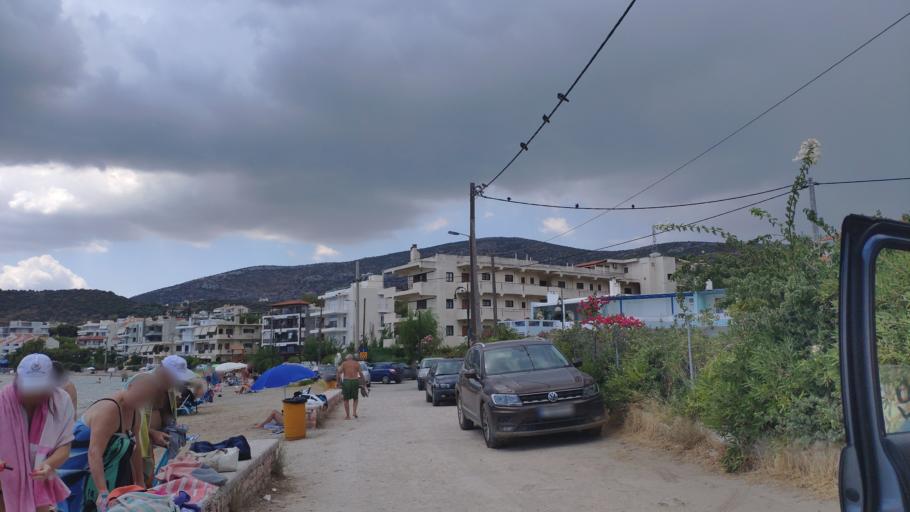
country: GR
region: Attica
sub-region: Nomarchia Anatolikis Attikis
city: Limin Mesoyaias
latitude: 37.8840
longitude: 24.0148
